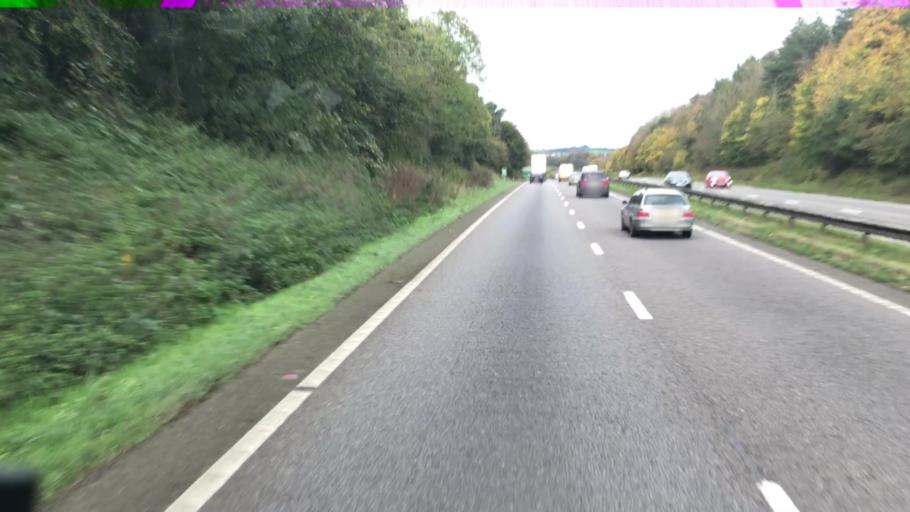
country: GB
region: England
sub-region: Devon
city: Exeter
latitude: 50.6933
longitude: -3.5395
